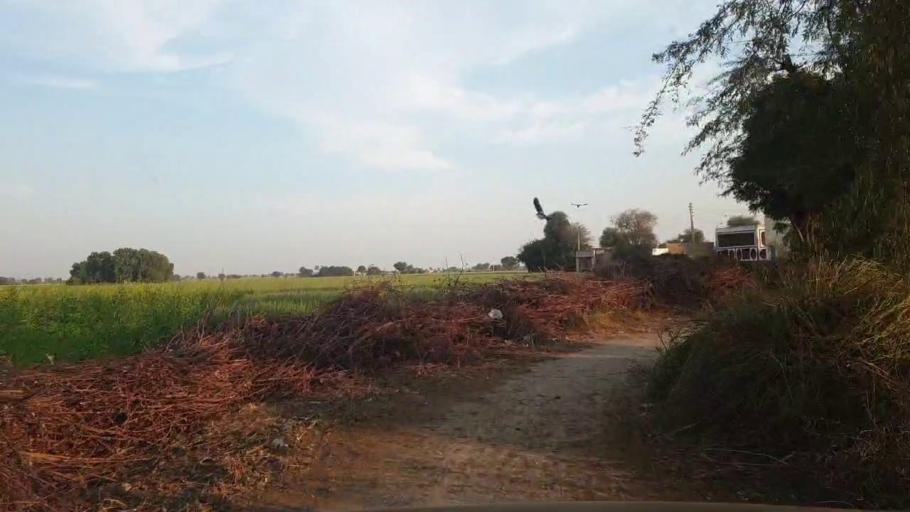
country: PK
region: Sindh
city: Shahpur Chakar
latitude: 26.1712
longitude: 68.6262
